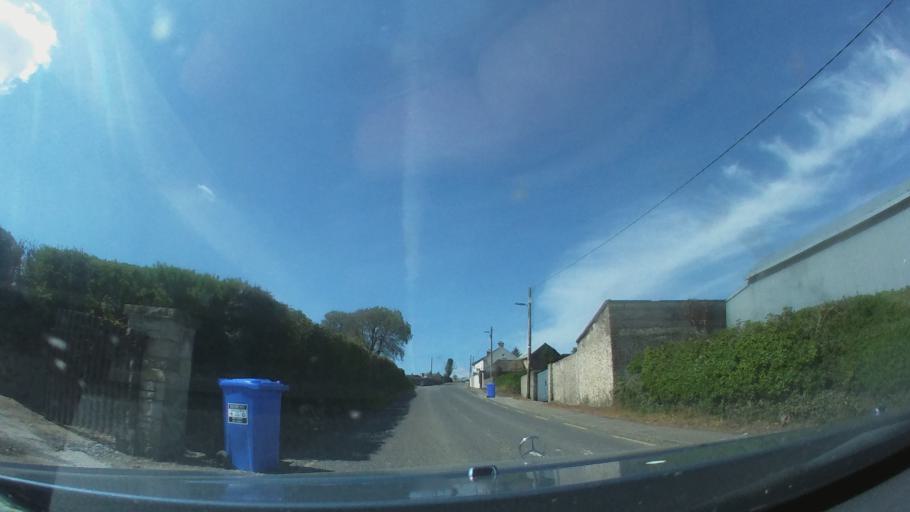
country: IE
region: Leinster
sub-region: Kilkenny
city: Callan
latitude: 52.6211
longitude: -7.4246
